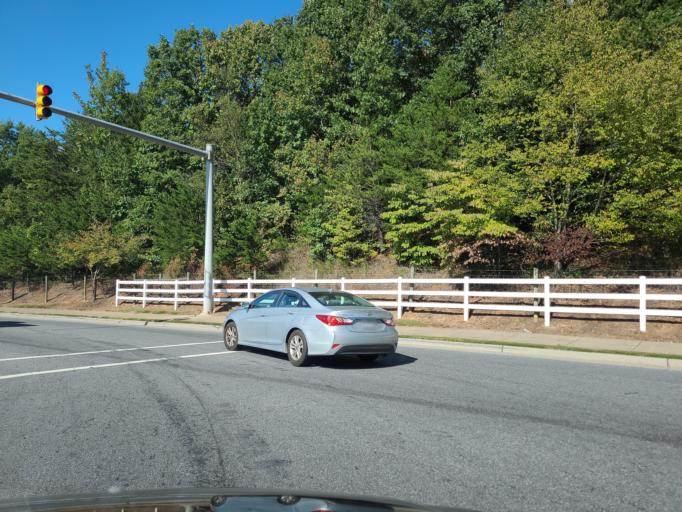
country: US
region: North Carolina
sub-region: Catawba County
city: Conover
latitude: 35.7220
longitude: -81.2040
